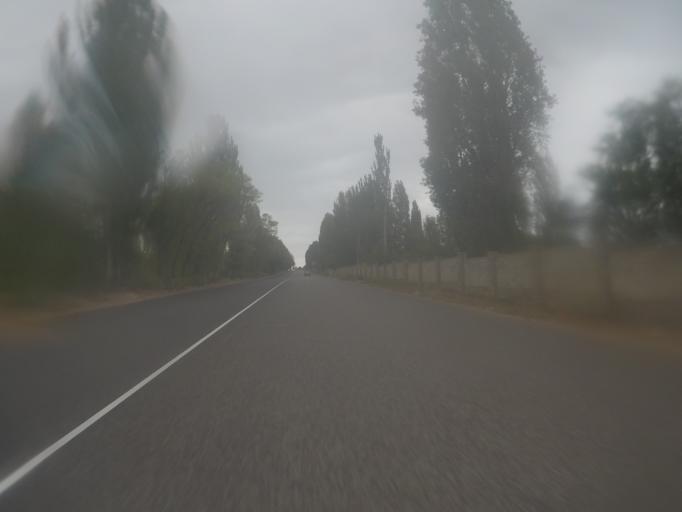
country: KG
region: Ysyk-Koel
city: Cholpon-Ata
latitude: 42.6695
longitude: 77.2771
